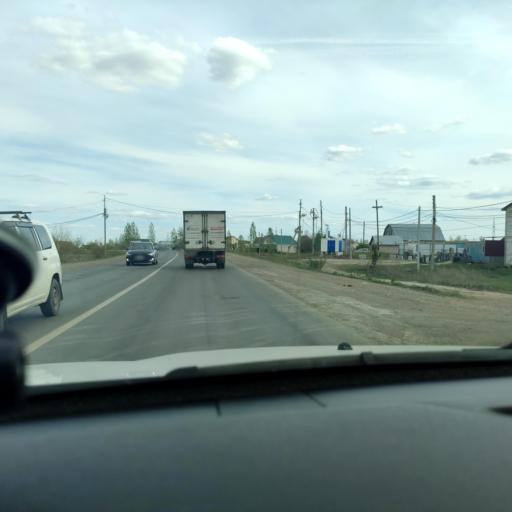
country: RU
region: Samara
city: Kinel'
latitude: 53.2115
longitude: 50.6185
